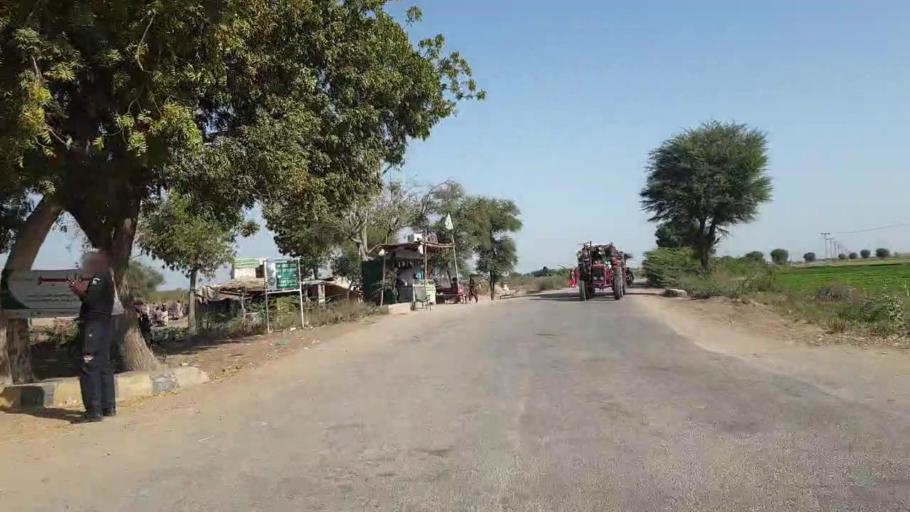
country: PK
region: Sindh
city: Umarkot
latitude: 25.4130
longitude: 69.7305
